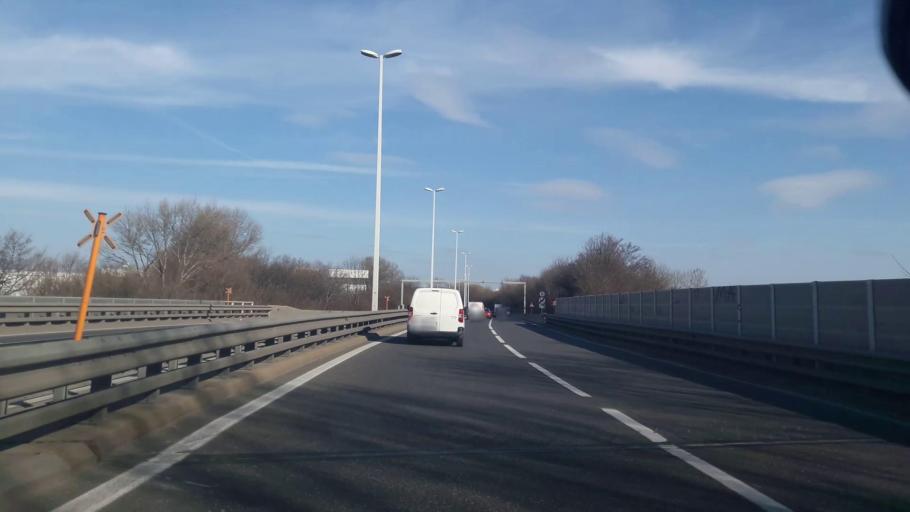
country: AT
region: Lower Austria
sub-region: Politischer Bezirk Korneuburg
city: Langenzersdorf
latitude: 48.2814
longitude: 16.3696
